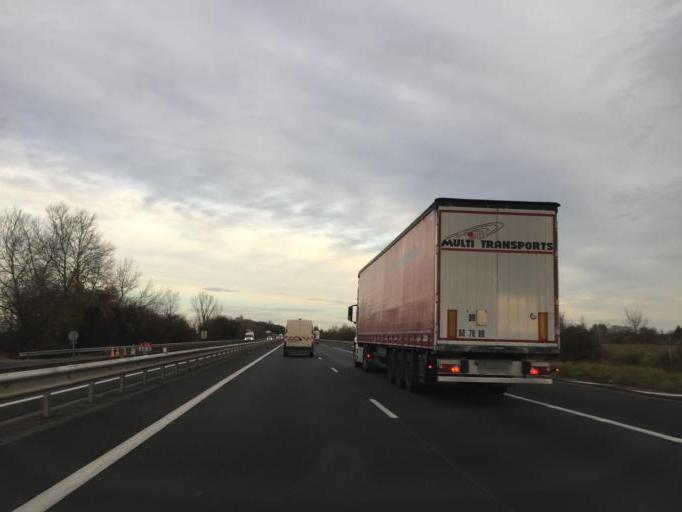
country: FR
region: Rhone-Alpes
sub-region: Departement du Rhone
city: Rillieux-la-Pape
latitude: 45.8460
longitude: 4.9129
